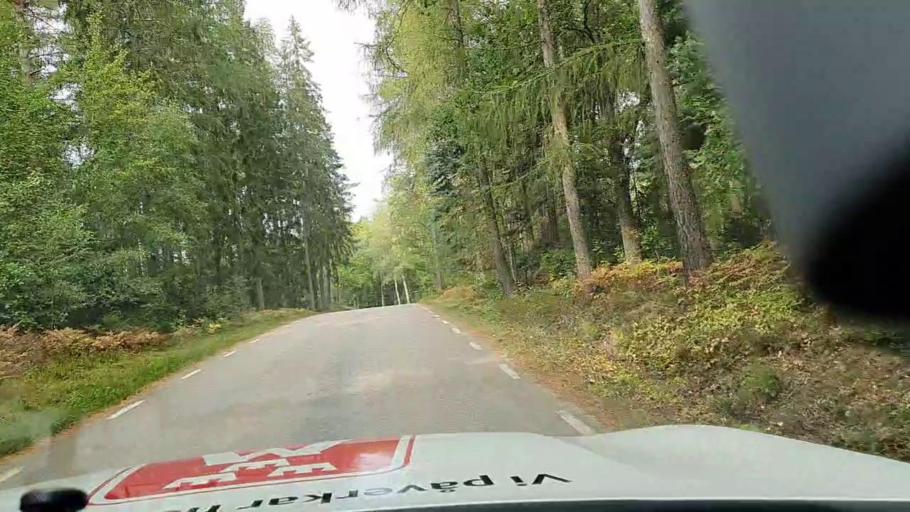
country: SE
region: Soedermanland
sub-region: Nykopings Kommun
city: Svalsta
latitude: 58.8304
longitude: 16.8811
